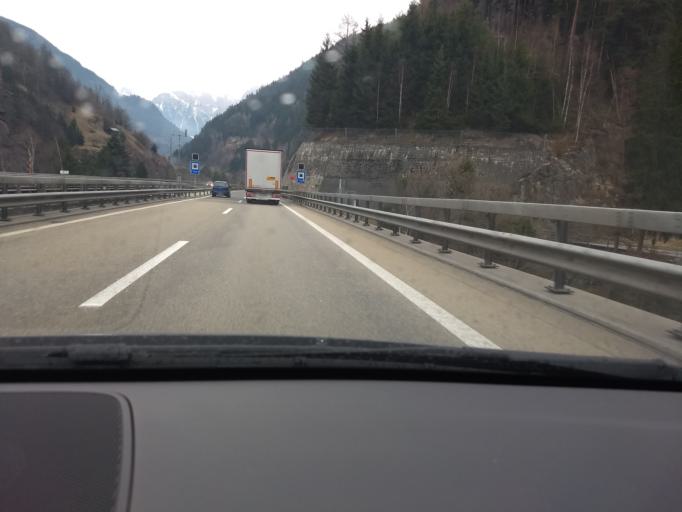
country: CH
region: Uri
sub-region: Uri
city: Silenen
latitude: 46.7407
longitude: 8.6392
